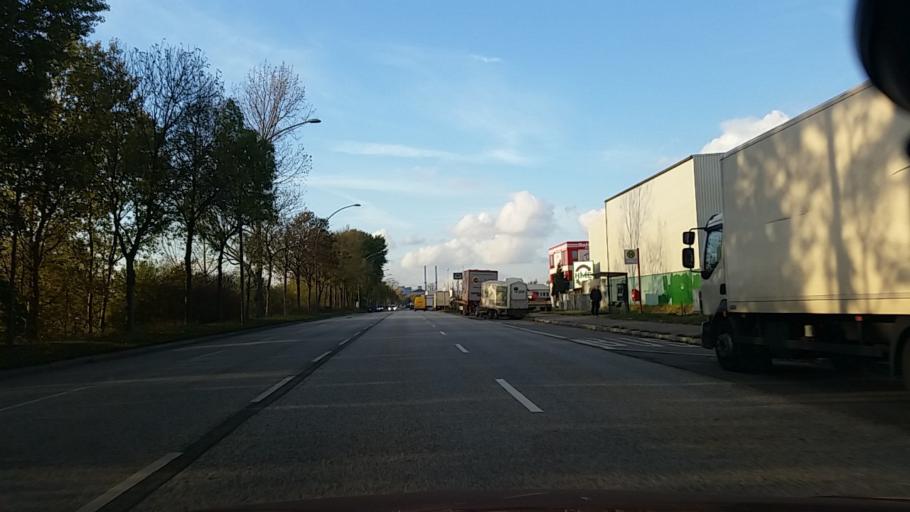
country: DE
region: Hamburg
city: Rothenburgsort
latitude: 53.5158
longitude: 10.0820
